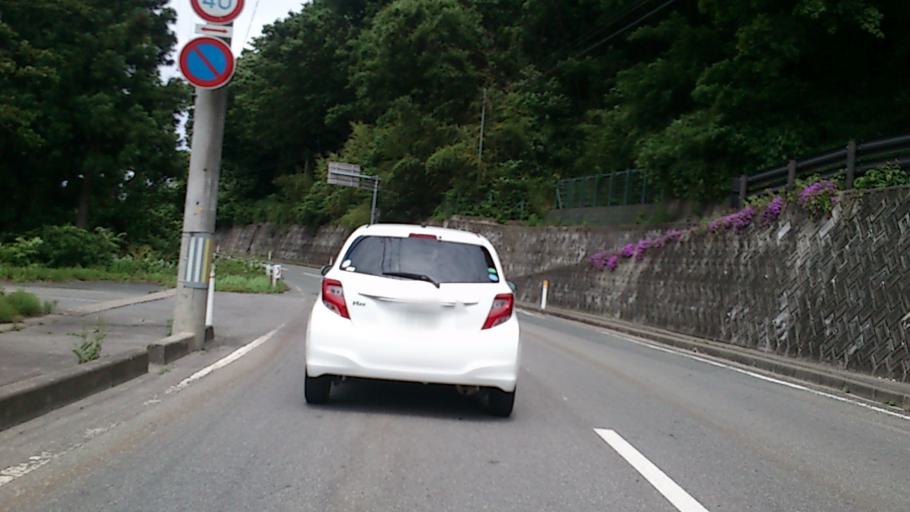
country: JP
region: Yamagata
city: Tendo
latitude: 38.3114
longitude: 140.4305
